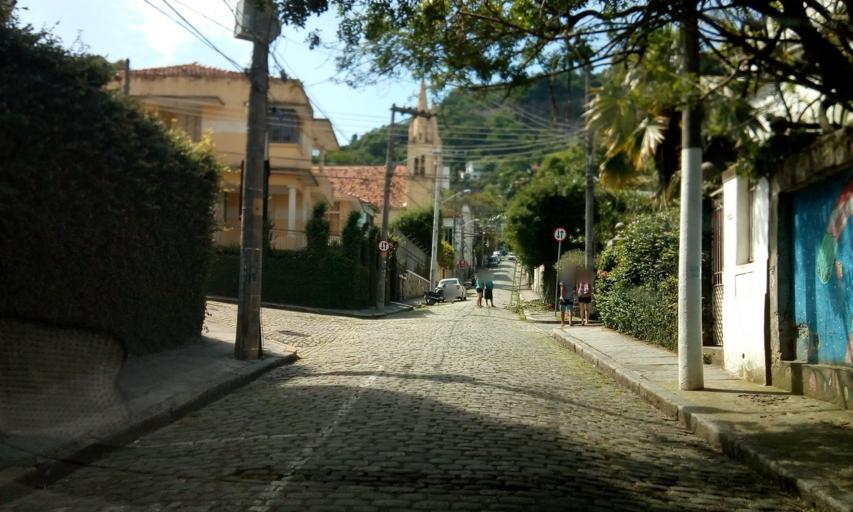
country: BR
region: Rio de Janeiro
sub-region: Rio De Janeiro
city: Rio de Janeiro
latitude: -22.9217
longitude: -43.1892
